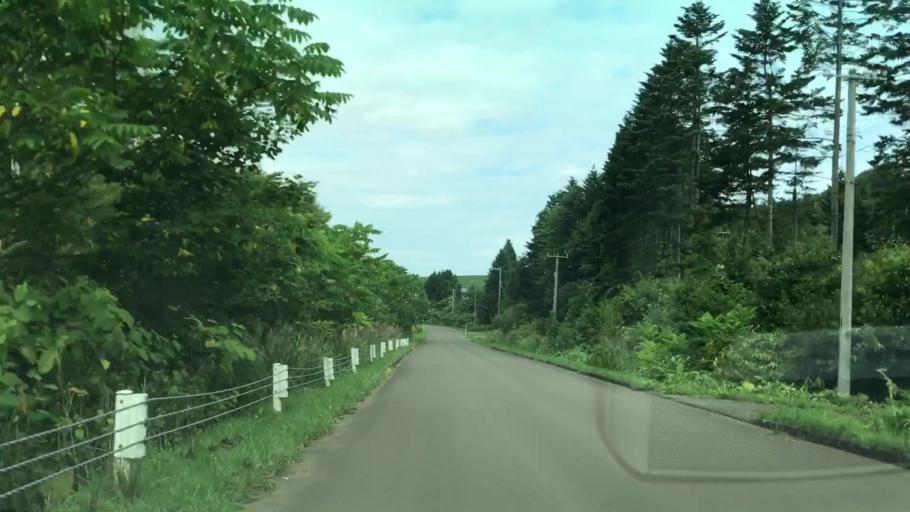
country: JP
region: Hokkaido
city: Yoichi
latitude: 43.1720
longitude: 140.8291
